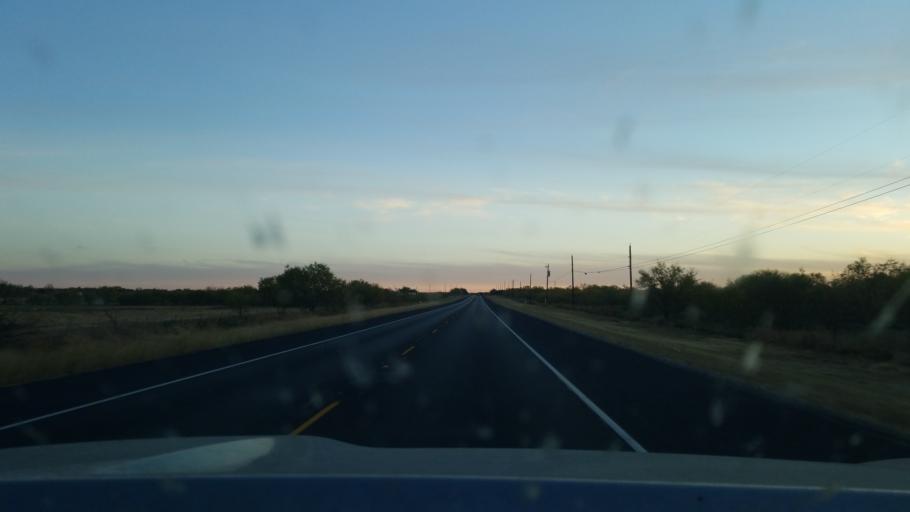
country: US
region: Texas
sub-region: Stephens County
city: Breckenridge
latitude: 32.6358
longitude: -98.9027
